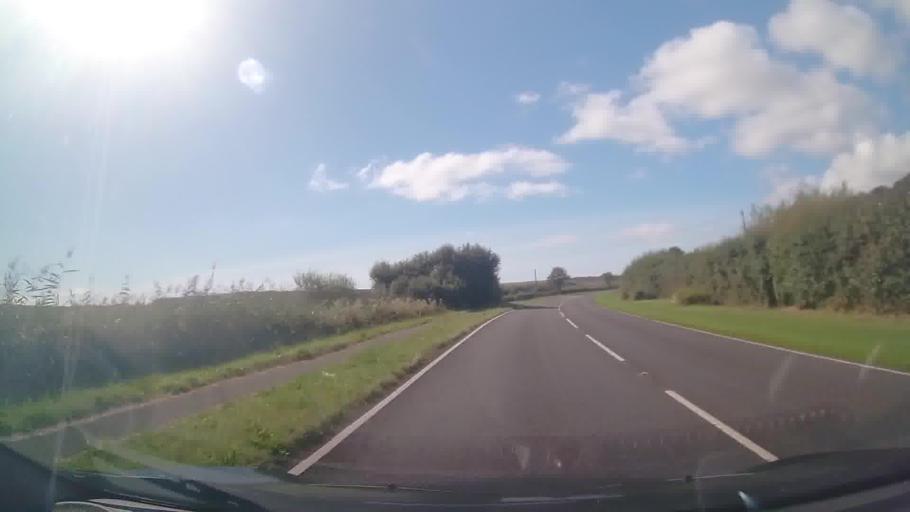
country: GB
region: Wales
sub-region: Pembrokeshire
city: Penally
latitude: 51.6621
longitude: -4.7194
